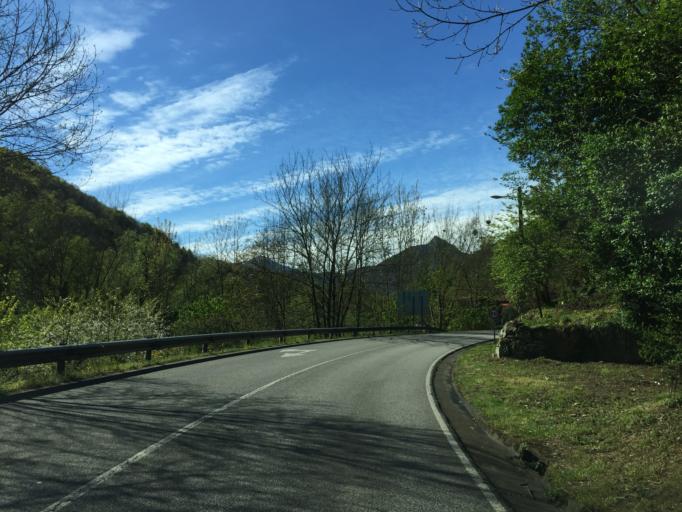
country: ES
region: Asturias
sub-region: Province of Asturias
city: Proaza
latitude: 43.3373
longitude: -5.9856
